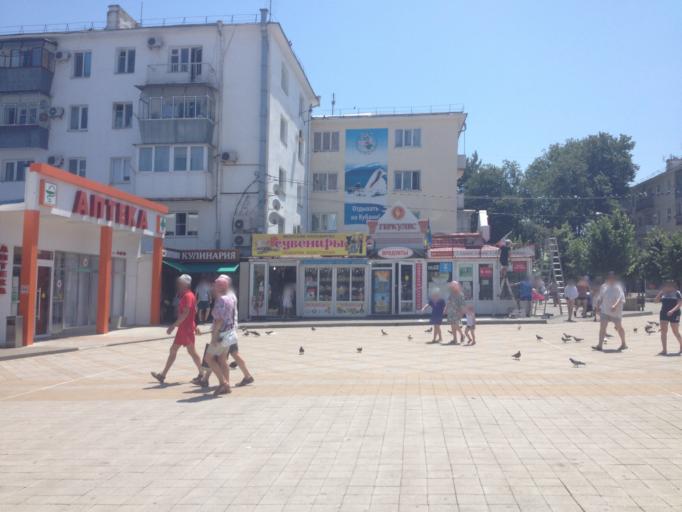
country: RU
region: Krasnodarskiy
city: Anapa
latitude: 44.8940
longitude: 37.3119
